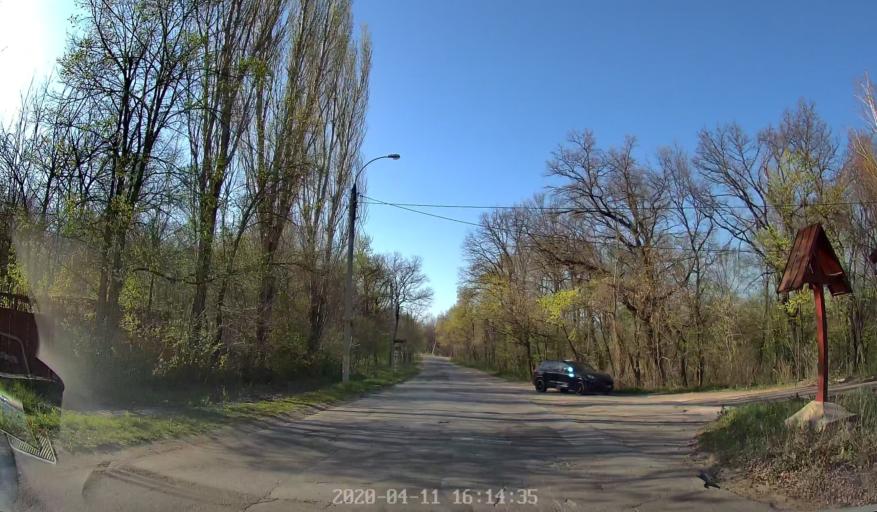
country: MD
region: Chisinau
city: Vadul lui Voda
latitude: 47.0762
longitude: 29.1001
